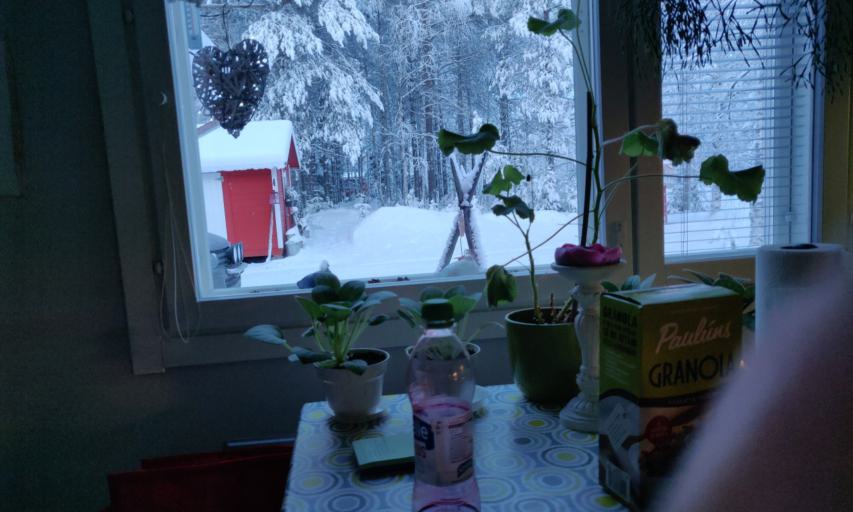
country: FI
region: Kainuu
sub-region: Kehys-Kainuu
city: Suomussalmi
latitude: 64.8992
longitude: 29.0226
